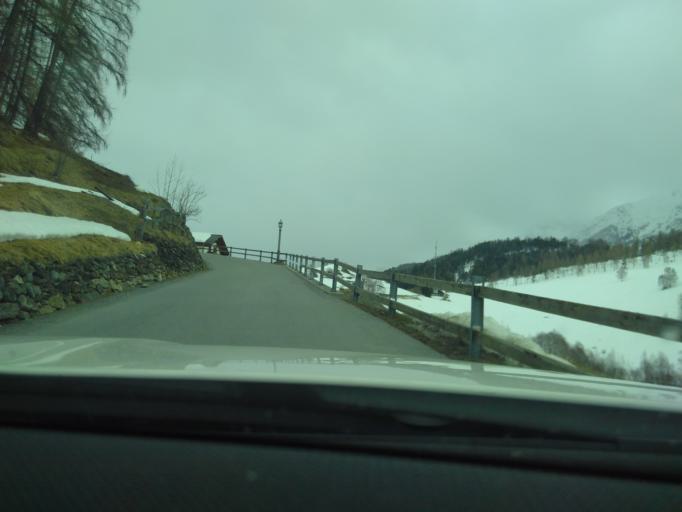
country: CH
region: Grisons
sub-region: Inn District
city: Scuol
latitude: 46.7778
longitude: 10.2617
